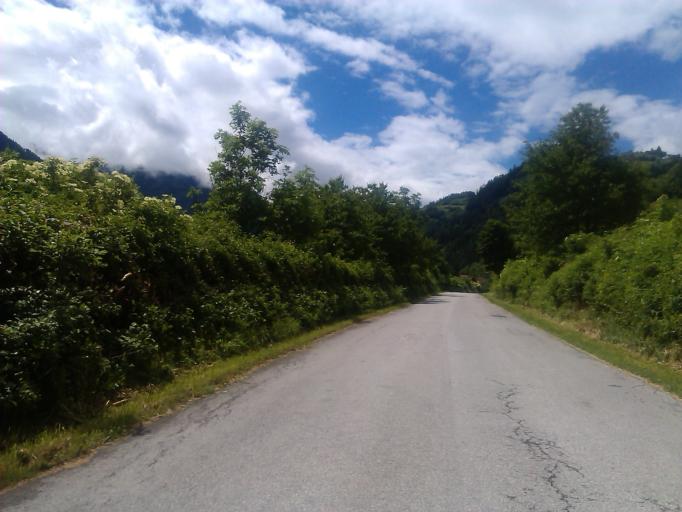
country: AT
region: Tyrol
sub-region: Politischer Bezirk Landeck
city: Prutz
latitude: 47.0879
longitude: 10.6625
